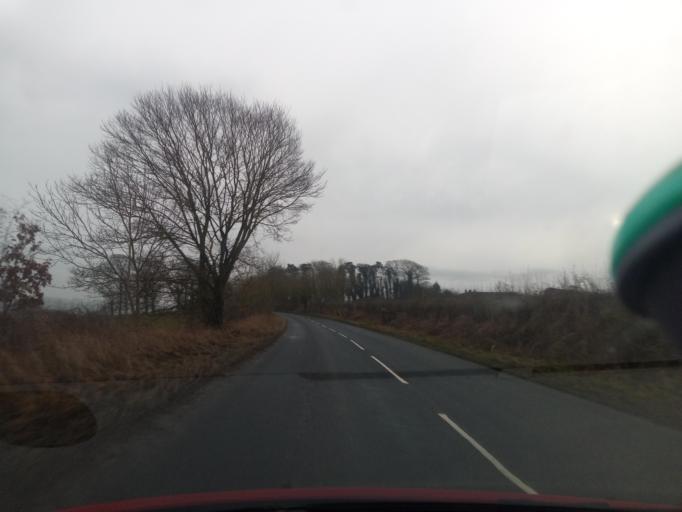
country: GB
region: England
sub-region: Northumberland
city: Birtley
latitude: 55.0468
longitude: -2.1544
